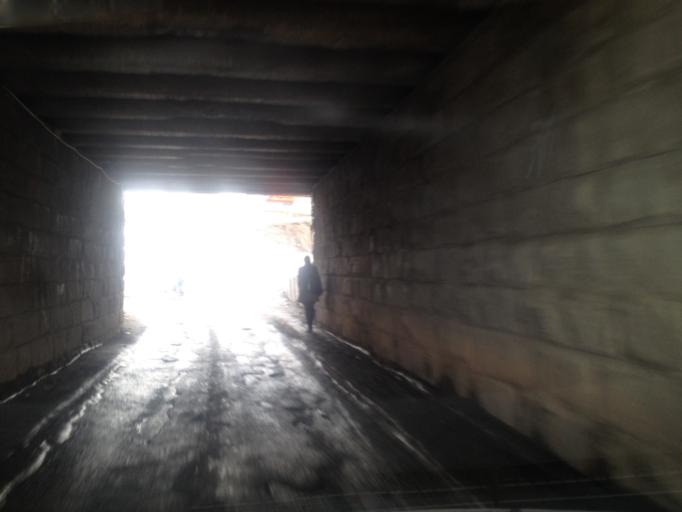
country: RU
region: Sverdlovsk
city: Yekaterinburg
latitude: 56.8589
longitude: 60.5804
